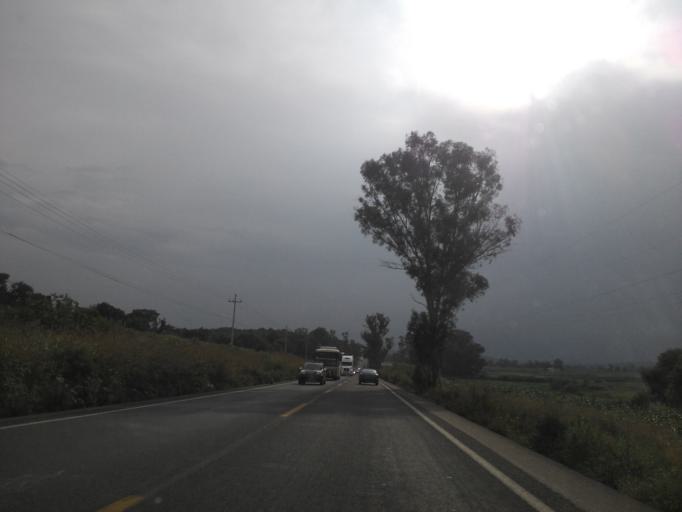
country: MX
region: Jalisco
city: Acatic
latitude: 20.7135
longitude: -102.9381
